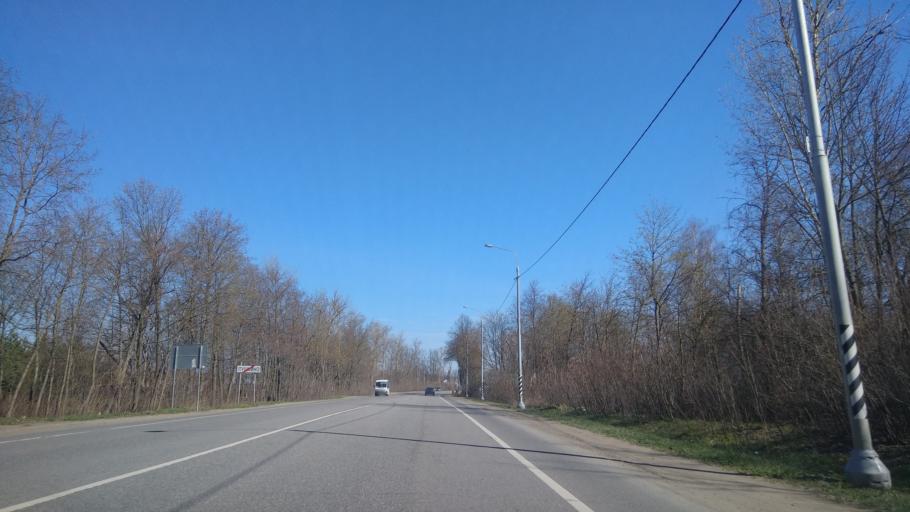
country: RU
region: Moskovskaya
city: Pushkino
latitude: 56.0391
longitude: 37.8703
